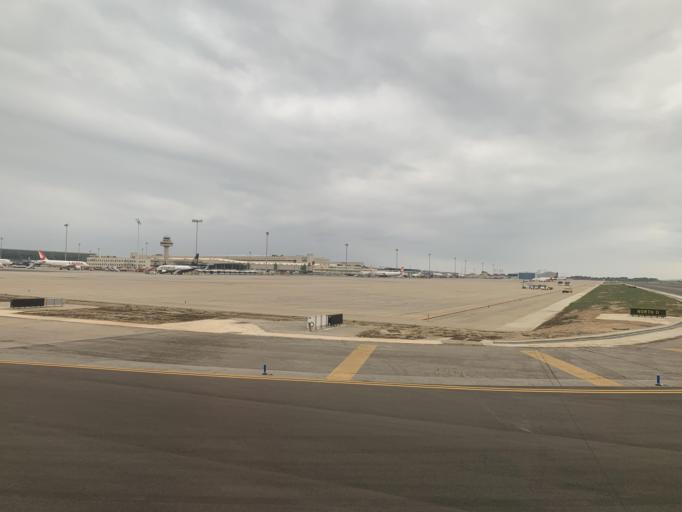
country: ES
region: Balearic Islands
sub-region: Illes Balears
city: s'Arenal
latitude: 39.5569
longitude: 2.7338
